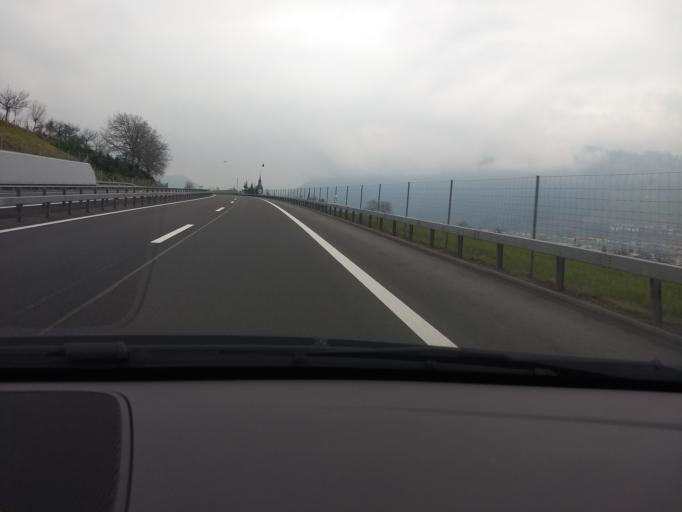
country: CH
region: Nidwalden
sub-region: Nidwalden
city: Buochs
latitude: 46.9719
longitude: 8.4283
